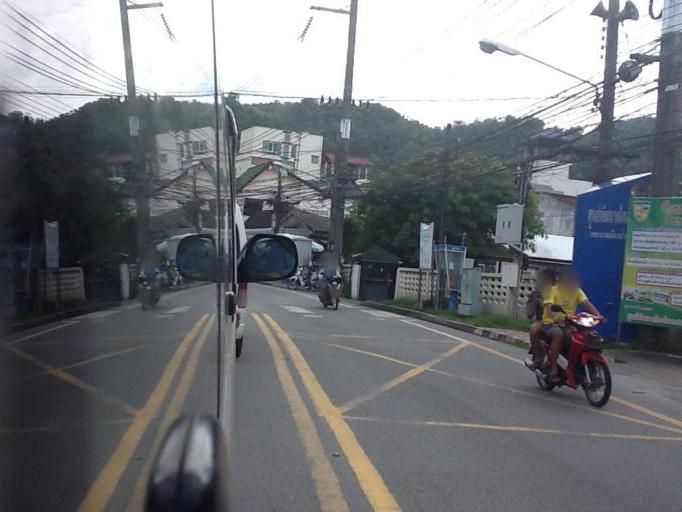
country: TH
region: Phuket
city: Patong
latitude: 7.9027
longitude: 98.3088
